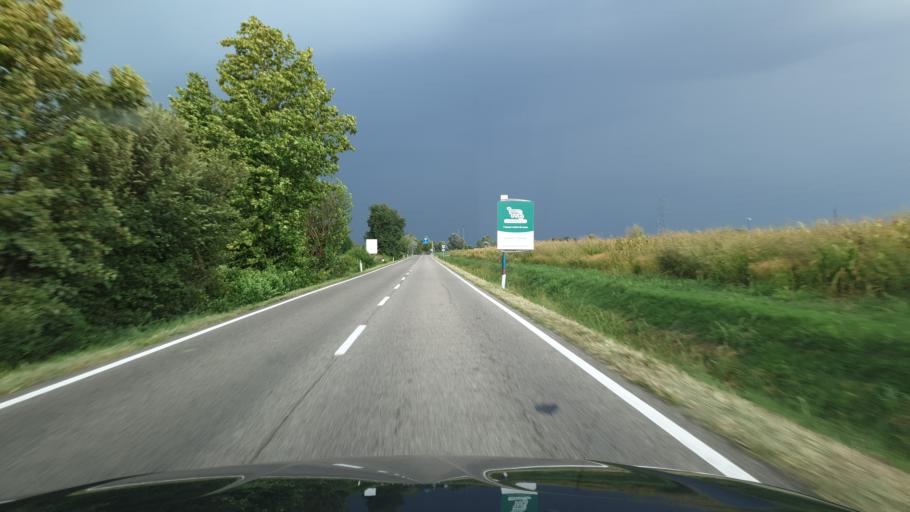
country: IT
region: Veneto
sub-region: Provincia di Vicenza
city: Noventa Vicentina
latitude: 45.2758
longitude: 11.5561
